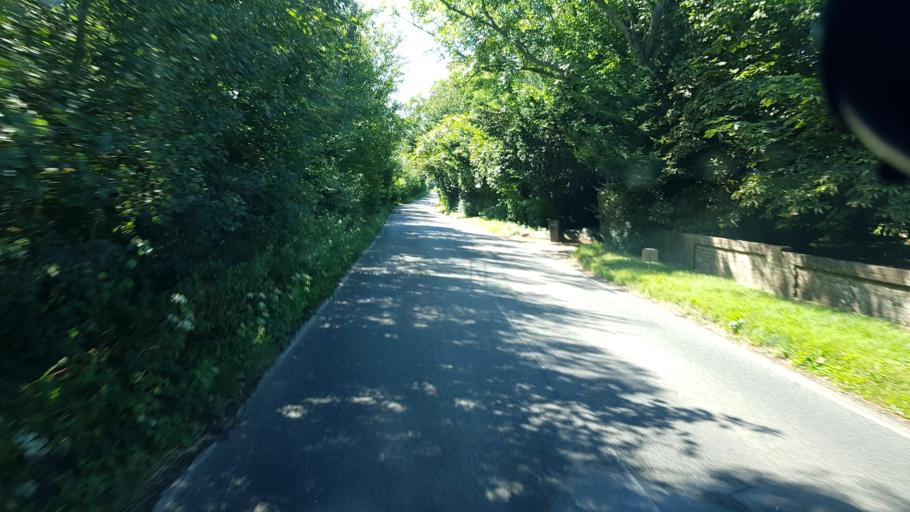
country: GB
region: England
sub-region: Kent
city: Edenbridge
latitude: 51.2021
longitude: 0.1272
